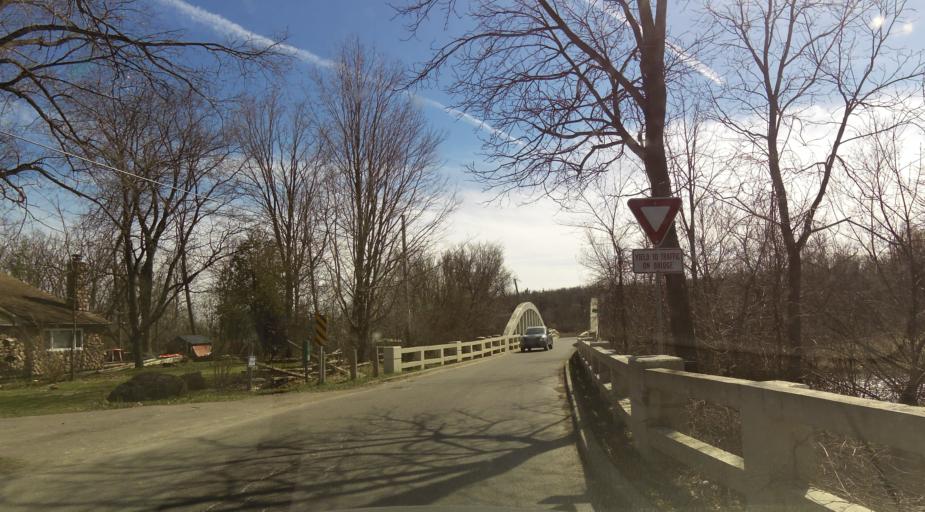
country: CA
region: Ontario
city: Brampton
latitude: 43.6433
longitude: -79.7701
